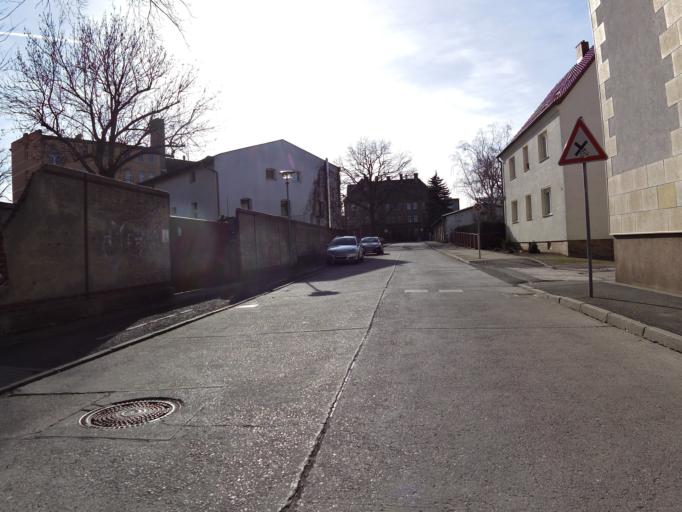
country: DE
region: Saxony
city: Torgau
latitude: 51.5619
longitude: 13.0026
